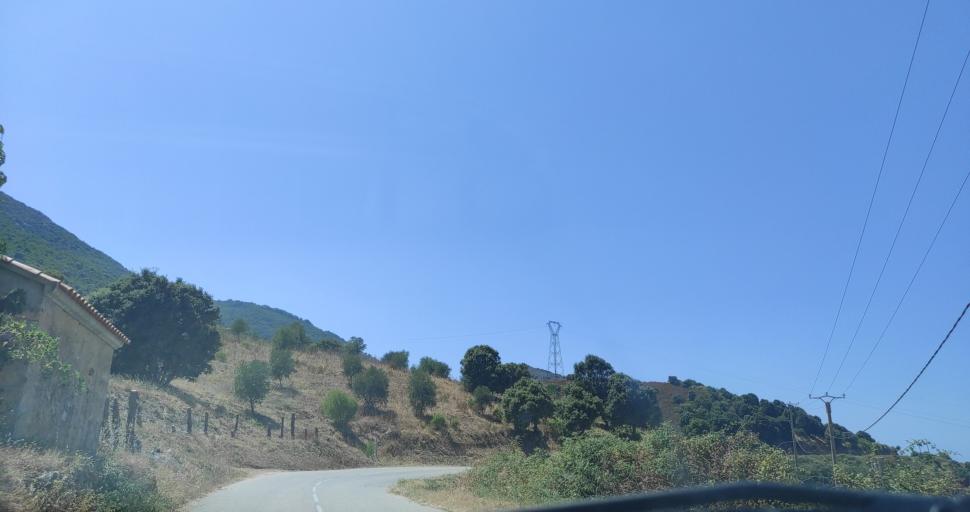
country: FR
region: Corsica
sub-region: Departement de la Corse-du-Sud
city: Alata
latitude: 41.9678
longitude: 8.7118
